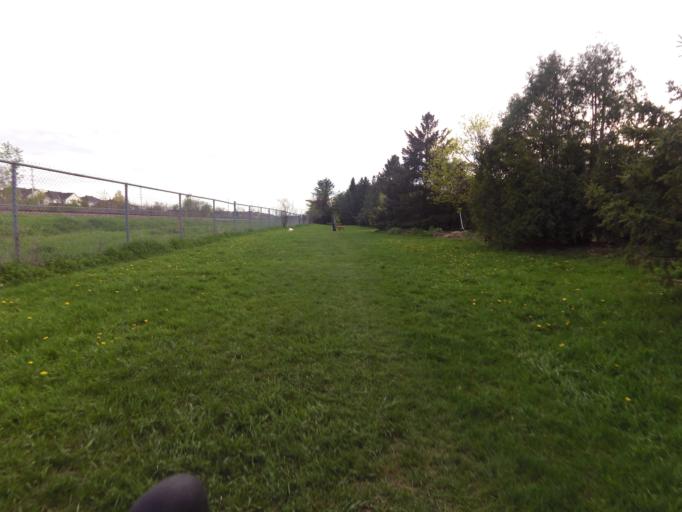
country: CA
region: Ontario
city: Bells Corners
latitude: 45.2912
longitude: -75.7433
